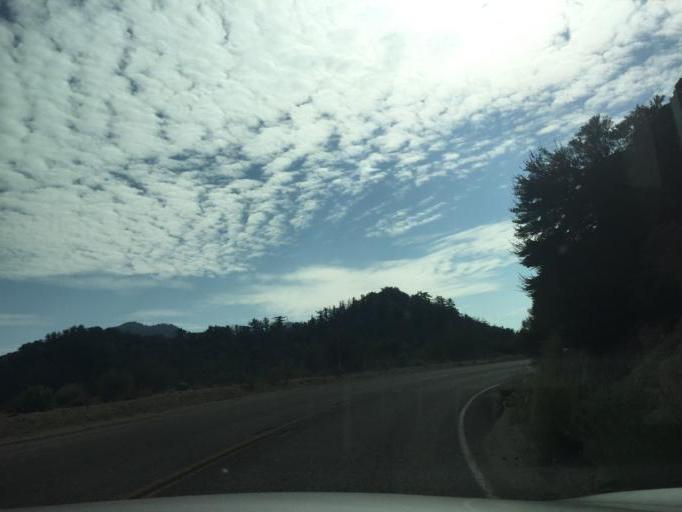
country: US
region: California
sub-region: Los Angeles County
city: Altadena
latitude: 34.2660
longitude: -118.0859
